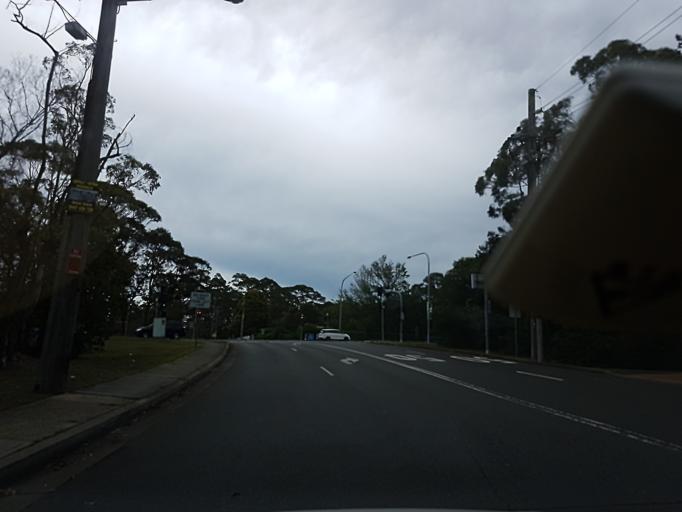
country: AU
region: New South Wales
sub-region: Warringah
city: Davidson
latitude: -33.7221
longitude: 151.2180
